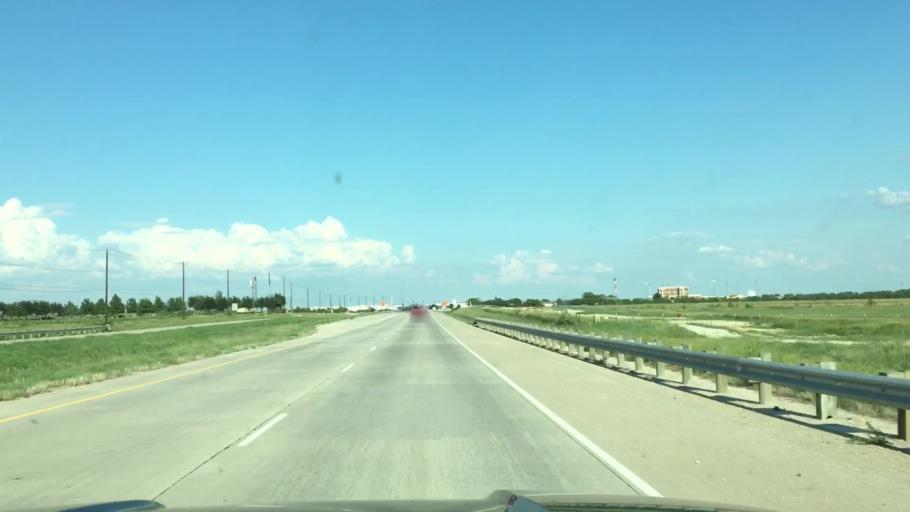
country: US
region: Texas
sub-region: Tarrant County
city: Haslet
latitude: 33.0352
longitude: -97.3333
